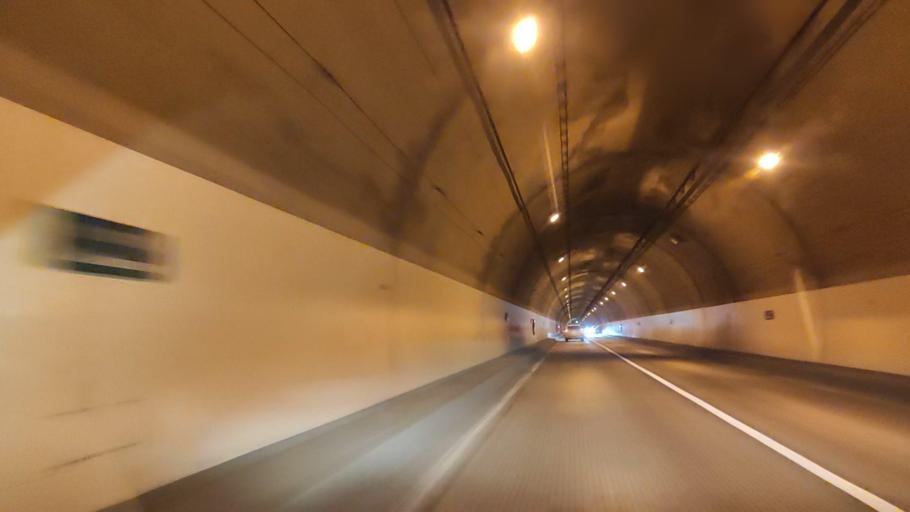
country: JP
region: Hokkaido
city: Ishikari
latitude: 43.4621
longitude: 141.4037
